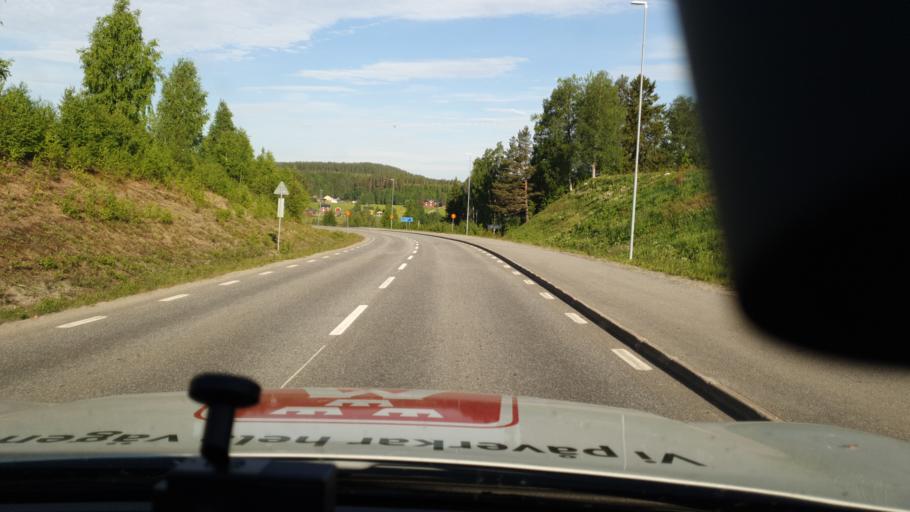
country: SE
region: Vaesterbotten
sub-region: Vindelns Kommun
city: Vindeln
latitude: 64.2001
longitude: 19.7090
